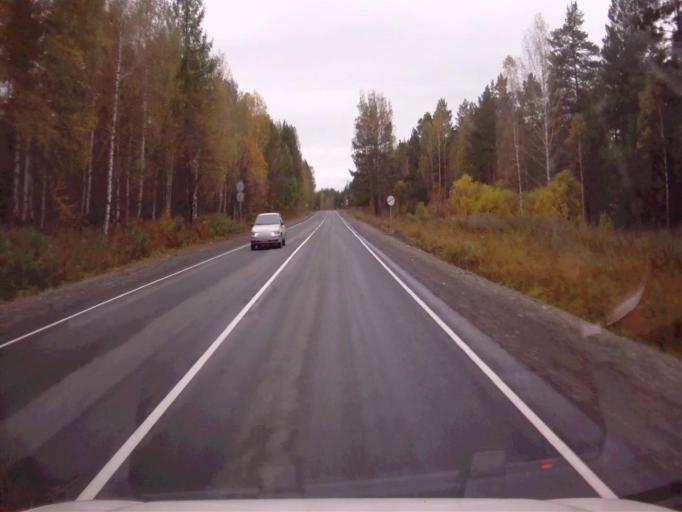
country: RU
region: Chelyabinsk
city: Nyazepetrovsk
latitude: 56.0579
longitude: 59.7339
